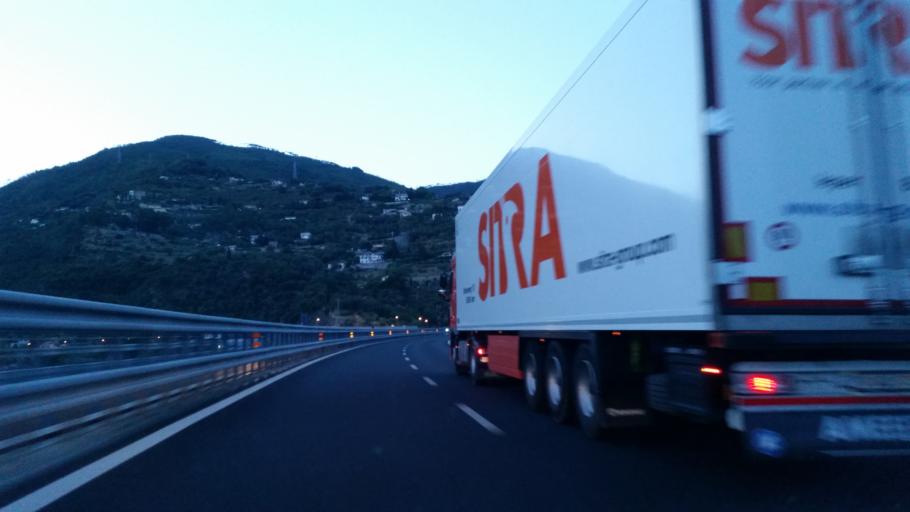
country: IT
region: Liguria
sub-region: Provincia di Imperia
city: San Remo
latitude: 43.8348
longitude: 7.7450
